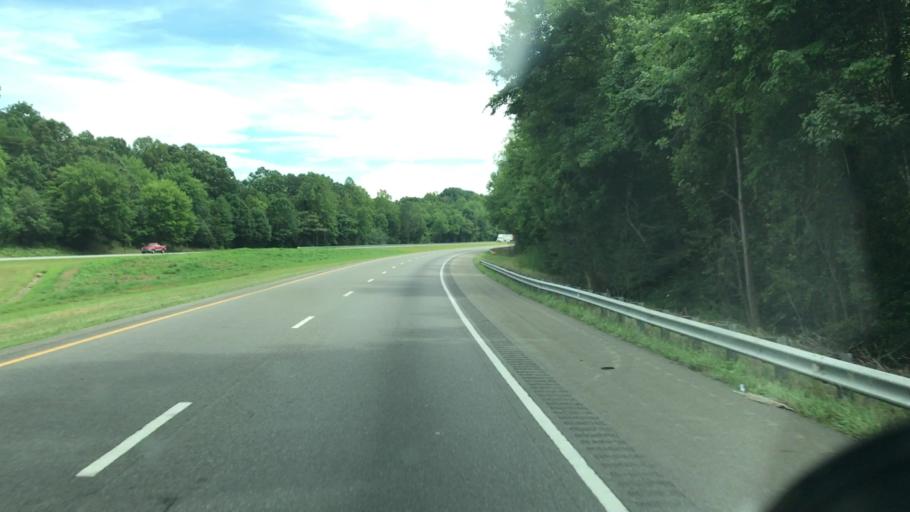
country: US
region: North Carolina
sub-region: Surry County
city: Dobson
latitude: 36.4292
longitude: -80.7765
